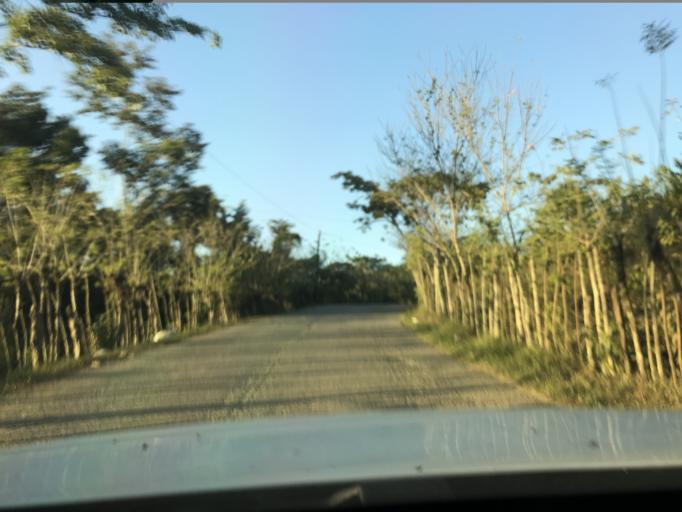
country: GT
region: Izabal
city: Morales
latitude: 15.6410
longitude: -89.0309
